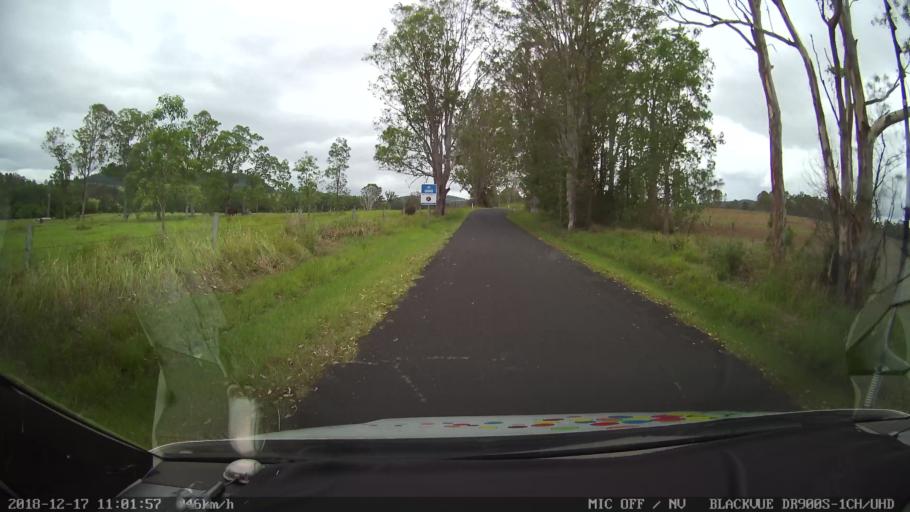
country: AU
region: New South Wales
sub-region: Richmond Valley
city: Casino
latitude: -28.8143
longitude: 152.6292
